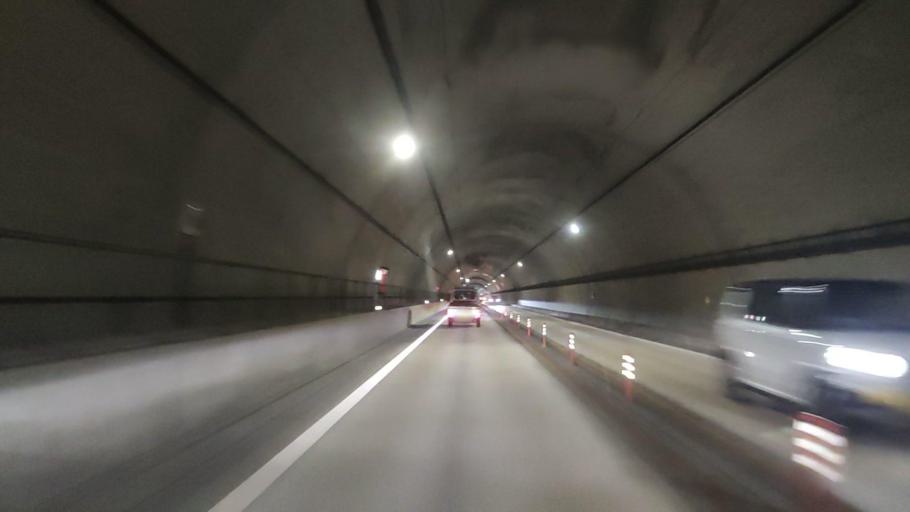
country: JP
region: Wakayama
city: Tanabe
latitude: 33.6263
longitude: 135.4167
